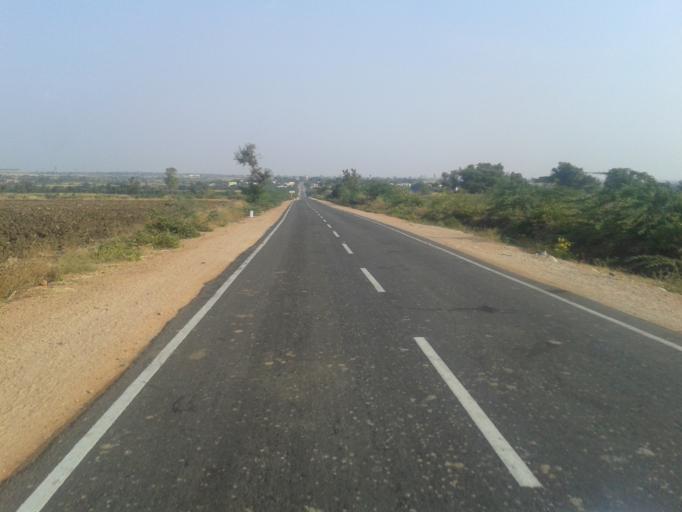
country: IN
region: Karnataka
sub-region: Raichur
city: Lingsugur
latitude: 16.2101
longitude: 76.6144
